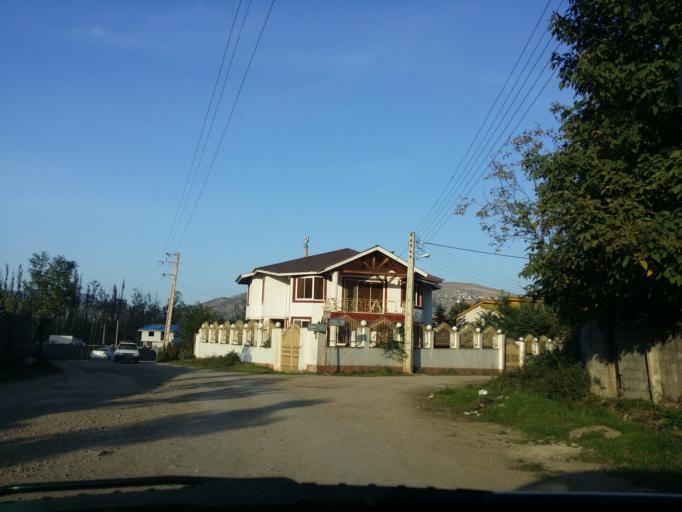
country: IR
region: Mazandaran
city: `Abbasabad
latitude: 36.5098
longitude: 51.1876
